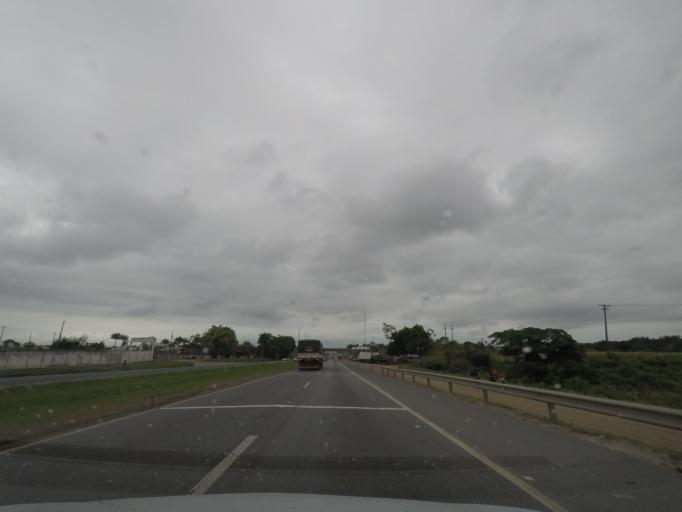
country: BR
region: Sao Paulo
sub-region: Registro
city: Registro
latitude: -24.4557
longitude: -47.8133
